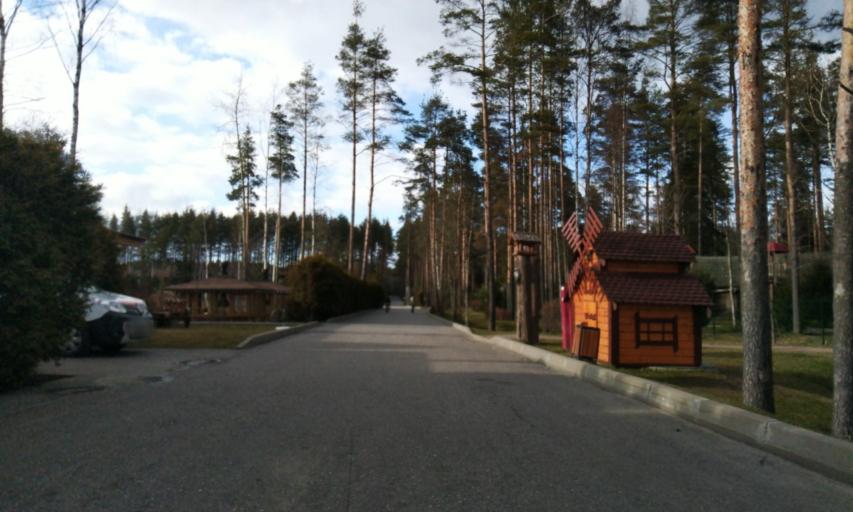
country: RU
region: Leningrad
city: Novoye Devyatkino
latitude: 60.1281
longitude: 30.4458
